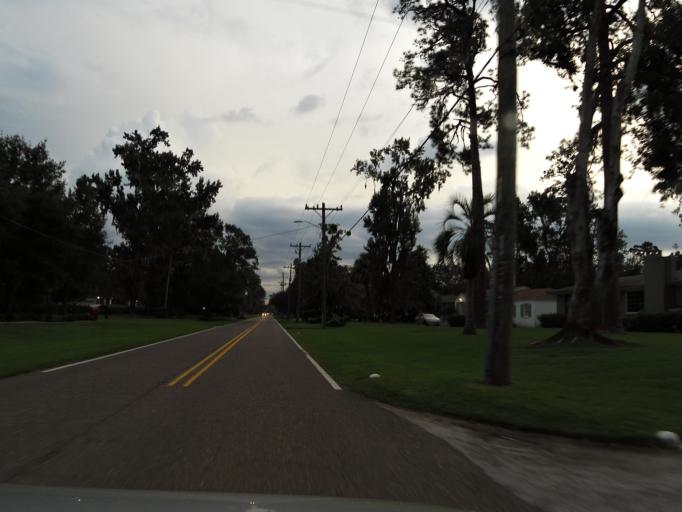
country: US
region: Florida
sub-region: Duval County
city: Jacksonville
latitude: 30.2586
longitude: -81.6978
